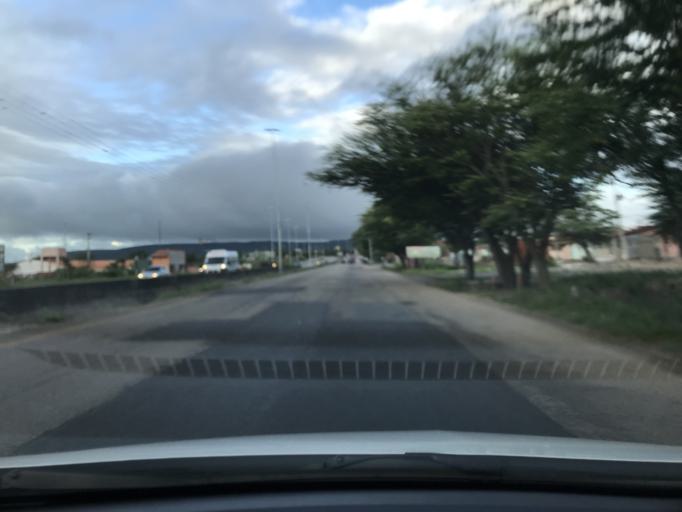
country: BR
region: Pernambuco
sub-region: Bezerros
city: Bezerros
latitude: -8.2998
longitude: -35.8525
